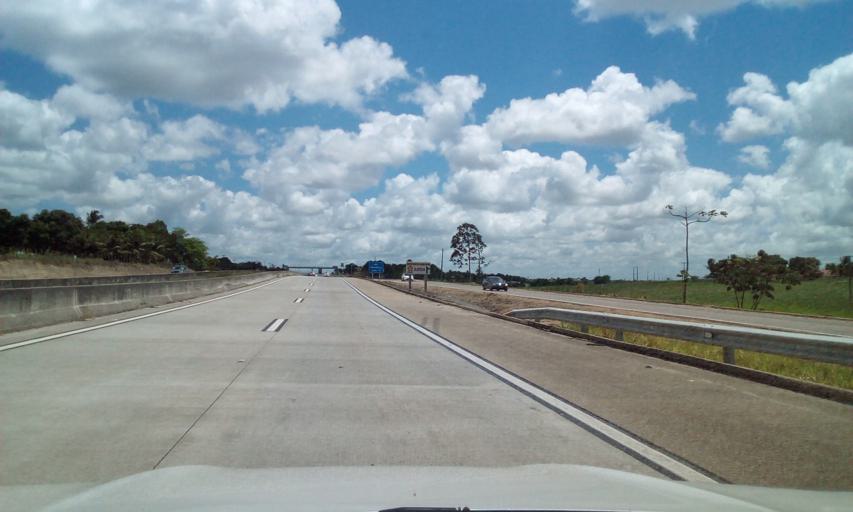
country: BR
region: Alagoas
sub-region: Junqueiro
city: Junqueiro
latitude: -9.8928
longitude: -36.3766
